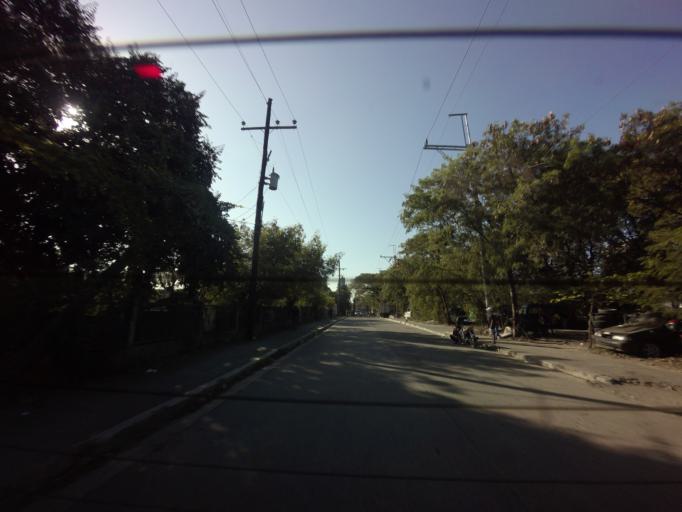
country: PH
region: Metro Manila
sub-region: Makati City
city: Makati City
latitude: 14.5314
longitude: 121.0351
